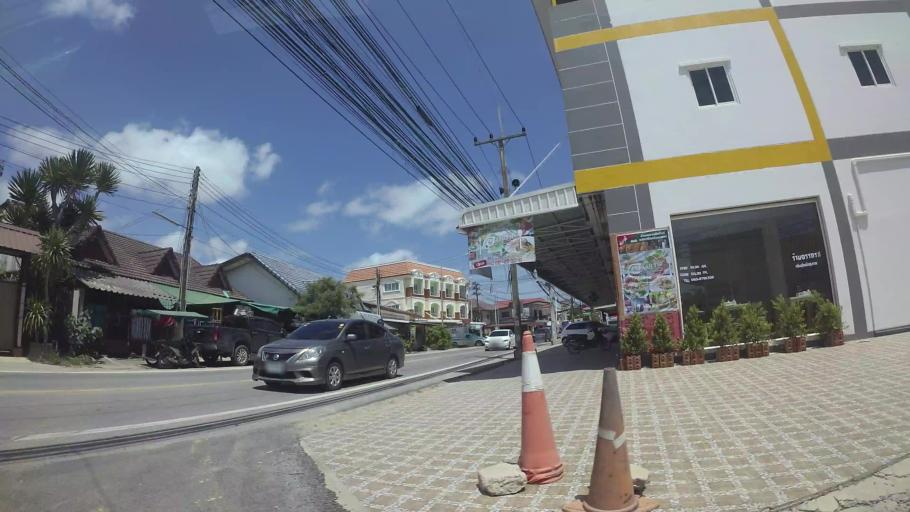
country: TH
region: Rayong
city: Rayong
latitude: 12.6908
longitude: 101.2691
